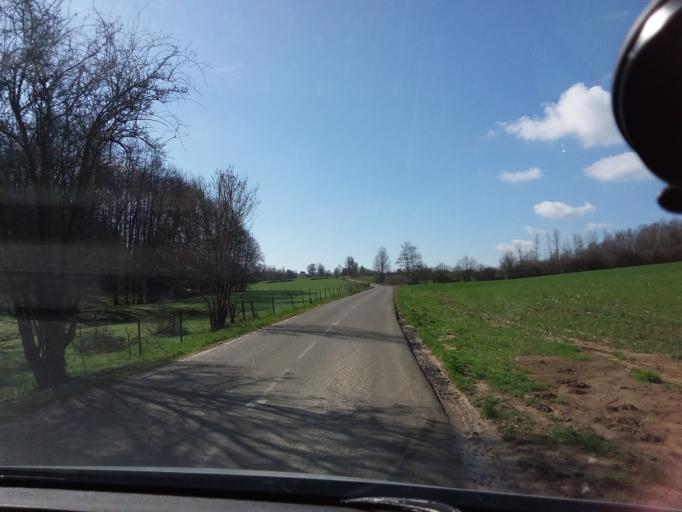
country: FR
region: Picardie
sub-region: Departement de l'Aisne
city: Hirson
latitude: 49.8652
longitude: 4.0898
